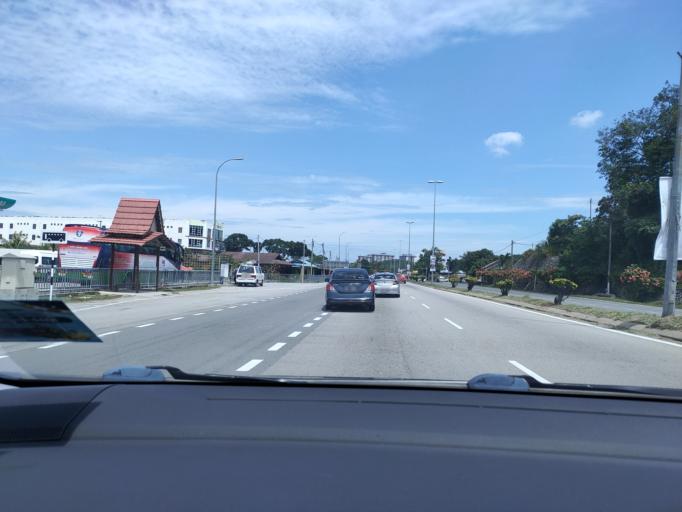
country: MY
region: Melaka
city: Batu Berendam
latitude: 2.2576
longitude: 102.2221
